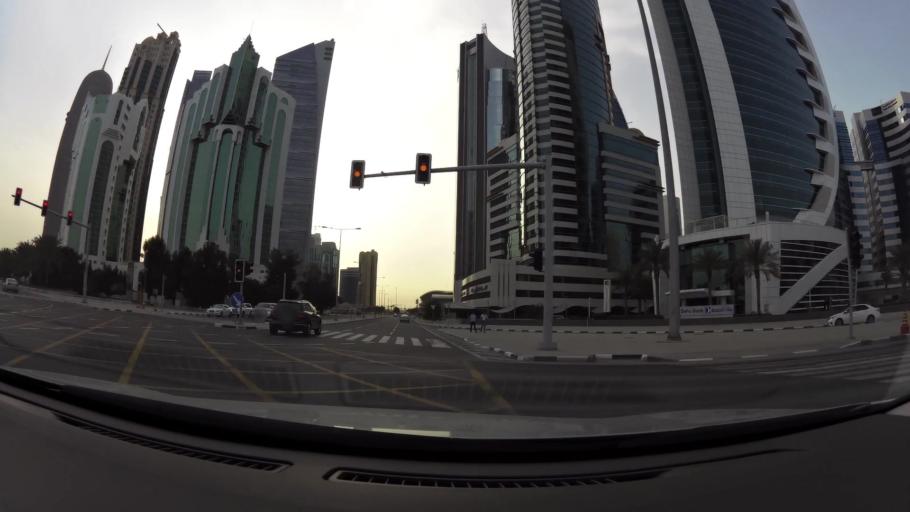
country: QA
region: Baladiyat ad Dawhah
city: Doha
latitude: 25.3193
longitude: 51.5319
